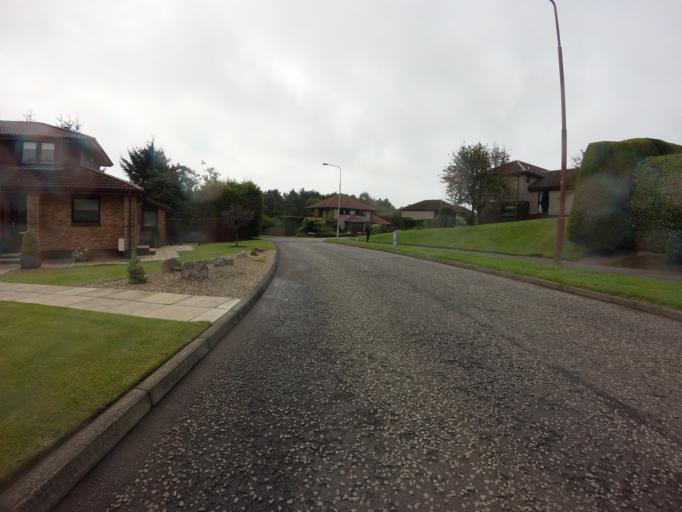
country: GB
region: Scotland
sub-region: West Lothian
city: Livingston
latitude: 55.9094
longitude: -3.5426
